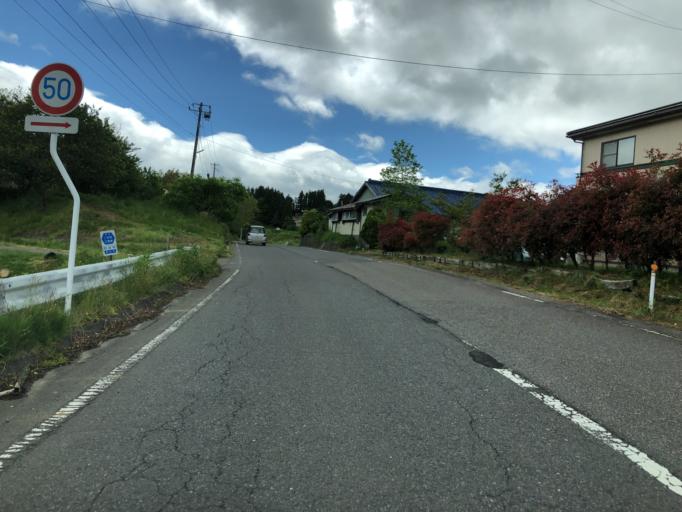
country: JP
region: Fukushima
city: Miharu
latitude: 37.4830
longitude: 140.4668
